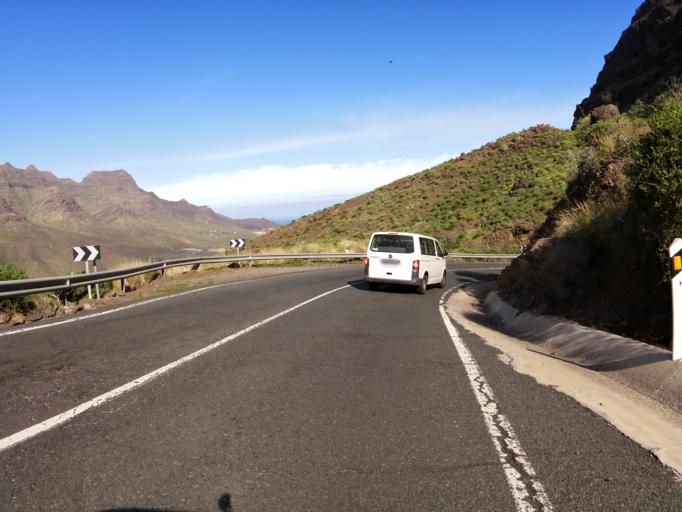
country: ES
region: Canary Islands
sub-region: Provincia de Las Palmas
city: San Nicolas
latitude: 27.9494
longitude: -15.7633
